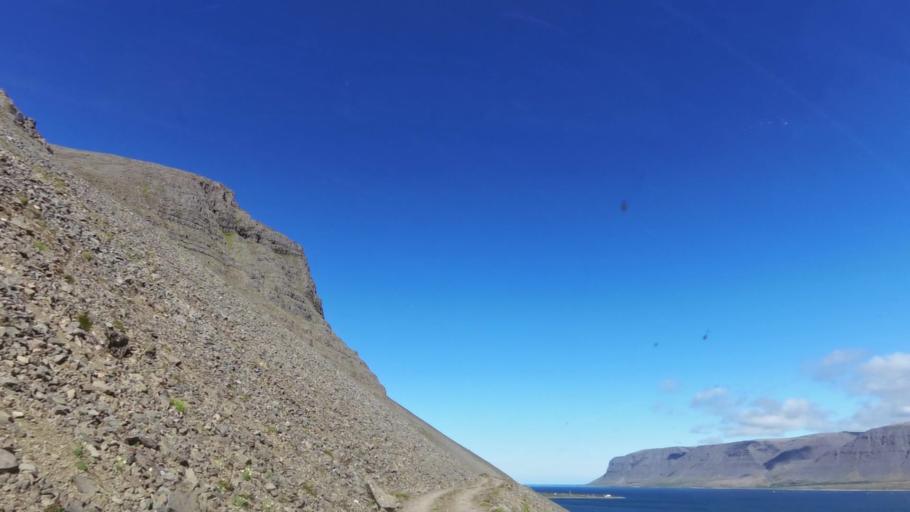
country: IS
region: West
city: Olafsvik
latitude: 65.6286
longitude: -23.9067
